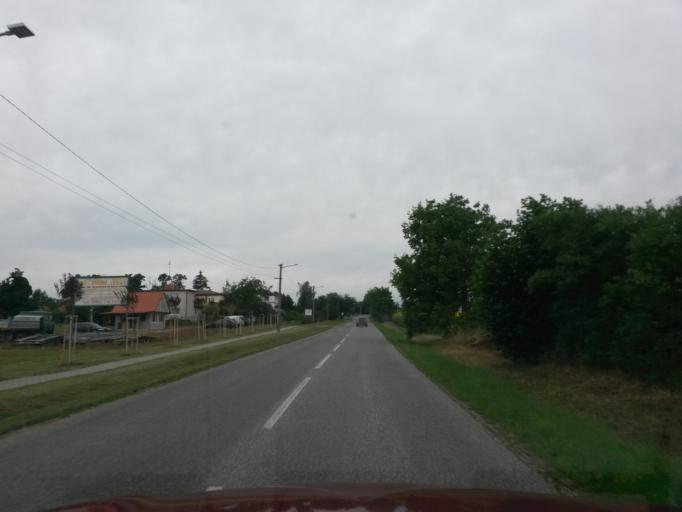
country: SK
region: Nitriansky
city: Tlmace
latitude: 48.1861
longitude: 18.4646
